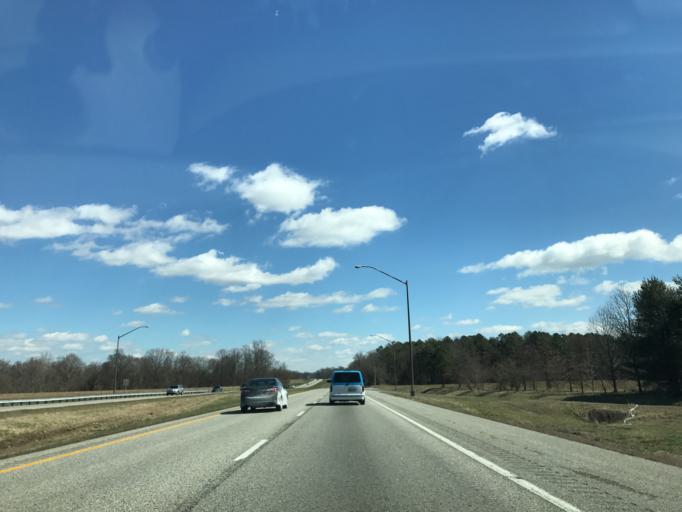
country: US
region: Maryland
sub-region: Queen Anne's County
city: Centreville
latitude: 39.0150
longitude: -76.0723
